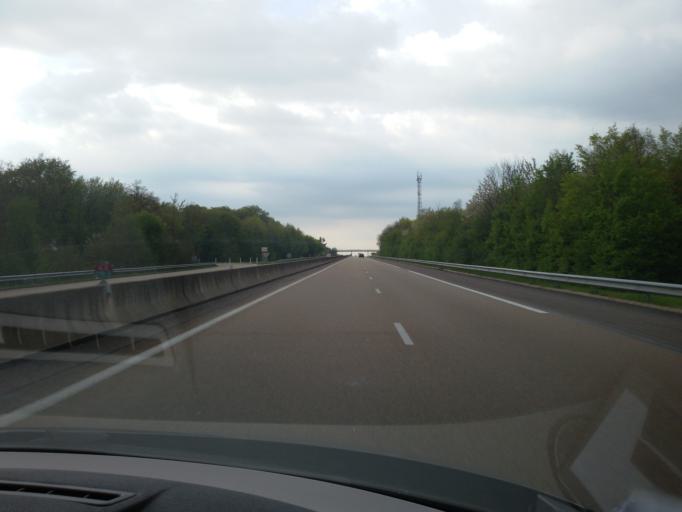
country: FR
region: Champagne-Ardenne
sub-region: Departement de la Haute-Marne
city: Chamarandes-Choignes
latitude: 47.9617
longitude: 5.1509
